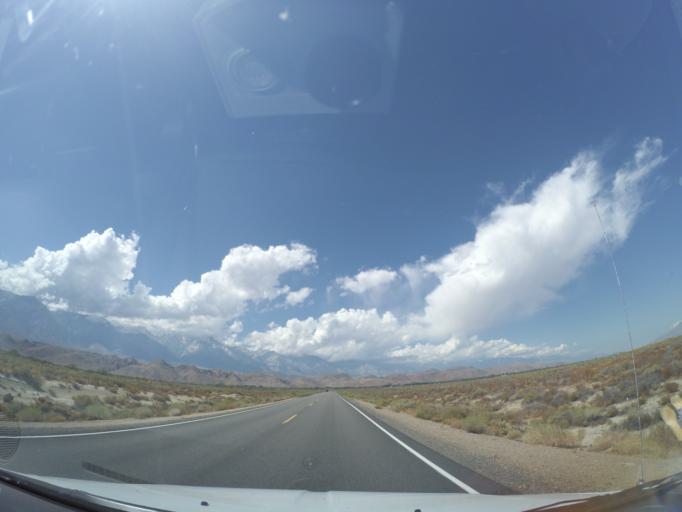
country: US
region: California
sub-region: Inyo County
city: Lone Pine
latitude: 36.5775
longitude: -118.0300
